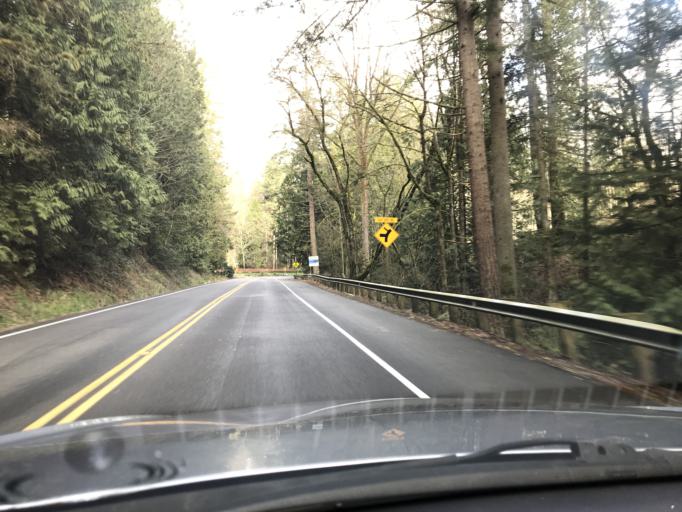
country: US
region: Washington
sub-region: King County
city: Ames Lake
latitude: 47.6339
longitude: -121.9881
